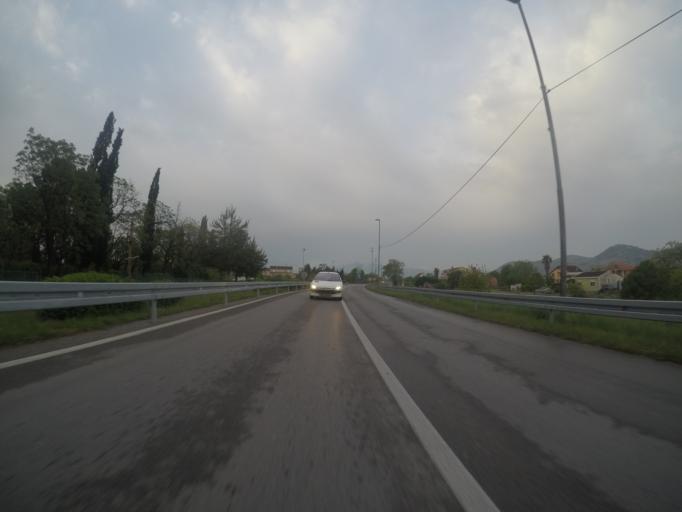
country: ME
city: Golubovci
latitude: 42.3276
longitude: 19.2201
